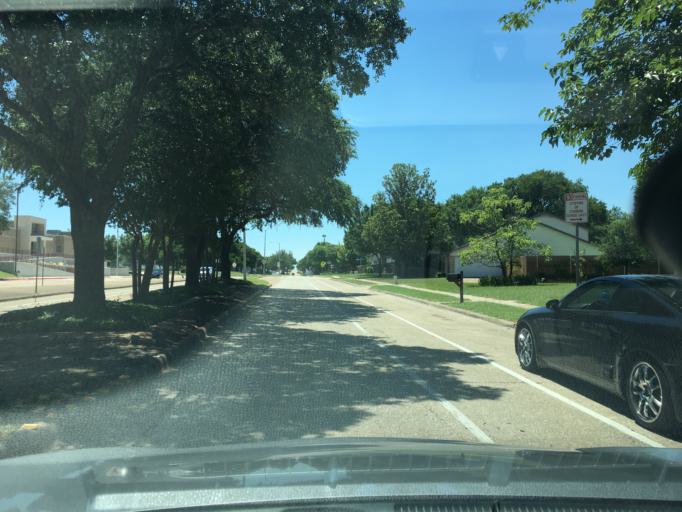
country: US
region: Texas
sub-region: Dallas County
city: Richardson
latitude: 32.9679
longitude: -96.6891
